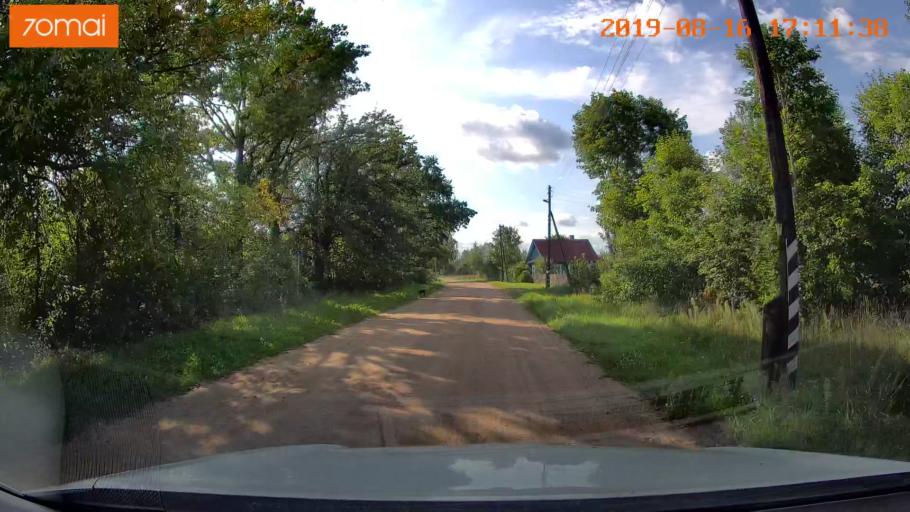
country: BY
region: Mogilev
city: Hlusha
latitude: 53.1963
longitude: 28.9032
